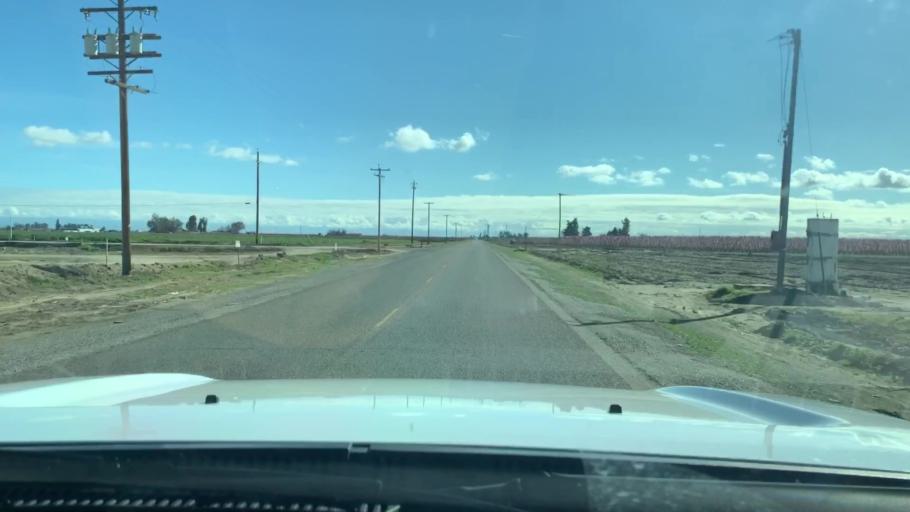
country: US
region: California
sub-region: Fresno County
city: Laton
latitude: 36.4893
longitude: -119.6959
